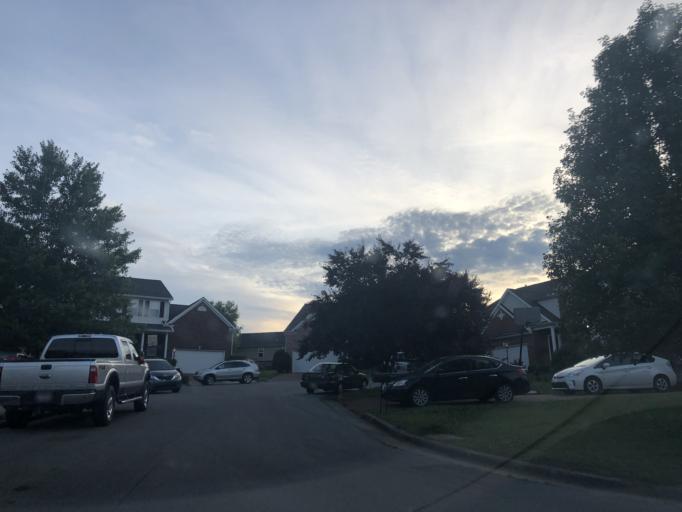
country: US
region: Tennessee
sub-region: Cheatham County
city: Pegram
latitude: 36.0478
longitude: -86.9569
